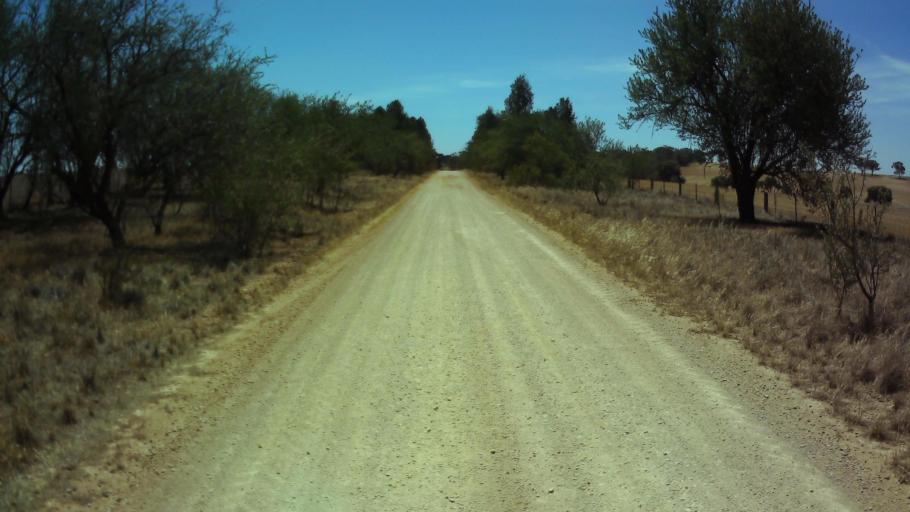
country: AU
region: New South Wales
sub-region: Weddin
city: Grenfell
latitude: -33.9274
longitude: 148.1786
